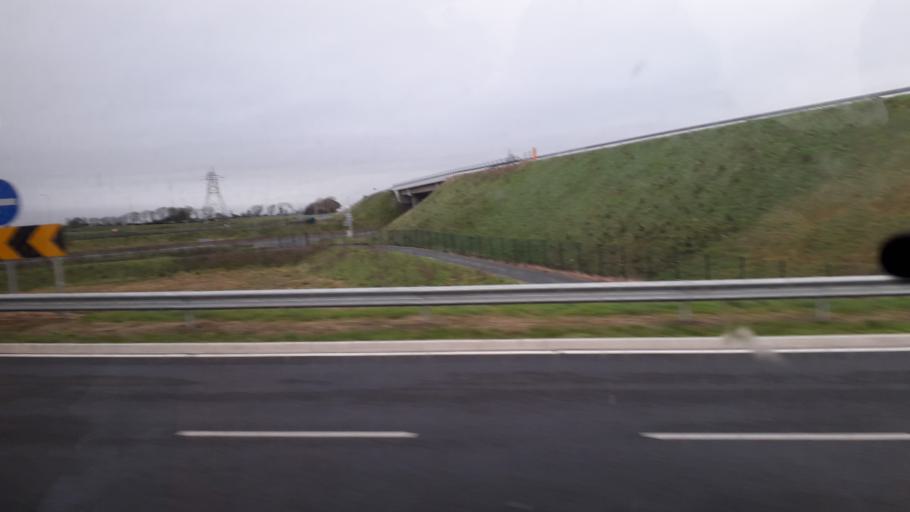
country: IE
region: Connaught
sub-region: County Galway
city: Athenry
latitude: 53.2959
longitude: -8.8087
